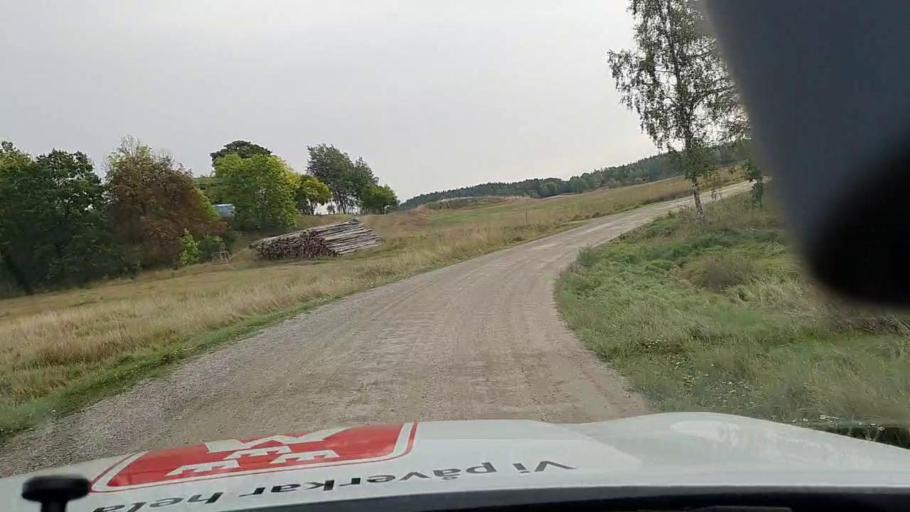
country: SE
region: Soedermanland
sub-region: Nykopings Kommun
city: Nykoping
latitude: 58.8991
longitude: 16.9868
